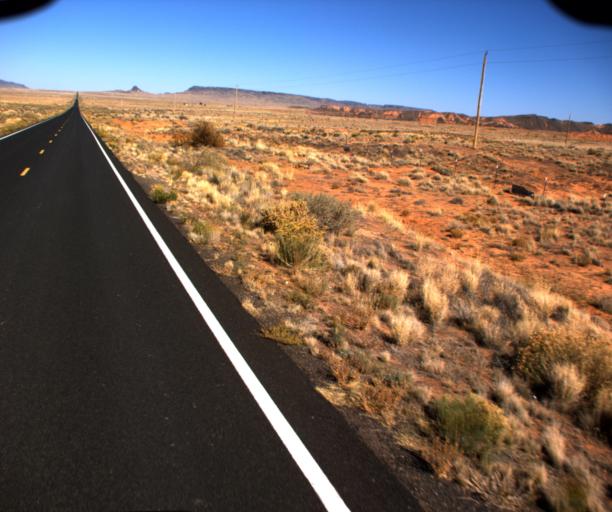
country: US
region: Arizona
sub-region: Navajo County
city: Dilkon
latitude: 35.3235
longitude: -110.4232
